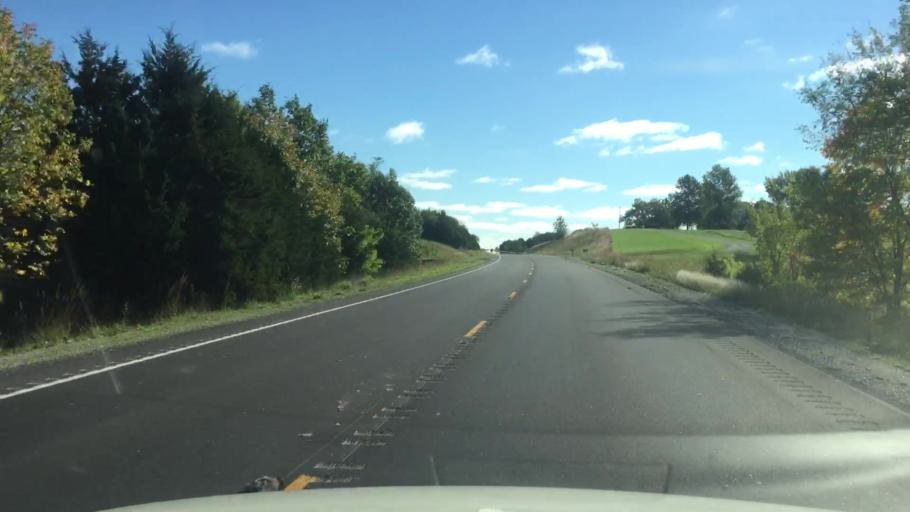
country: US
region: Missouri
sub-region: Boone County
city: Columbia
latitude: 38.9895
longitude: -92.5067
